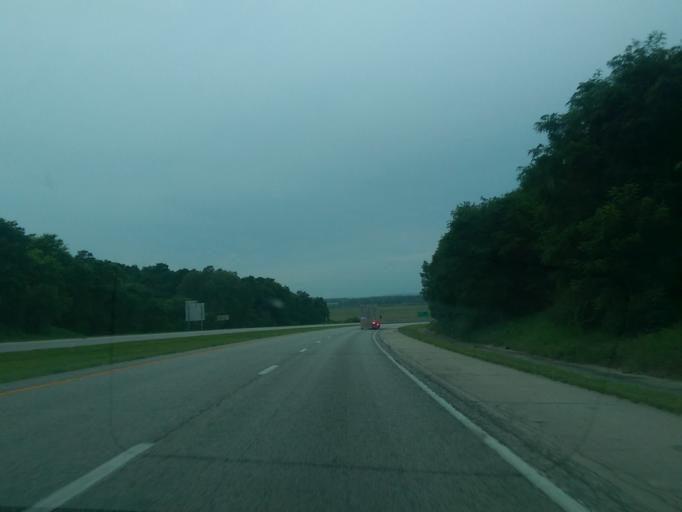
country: US
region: Missouri
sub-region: Holt County
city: Mound City
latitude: 40.0803
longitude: -95.2074
